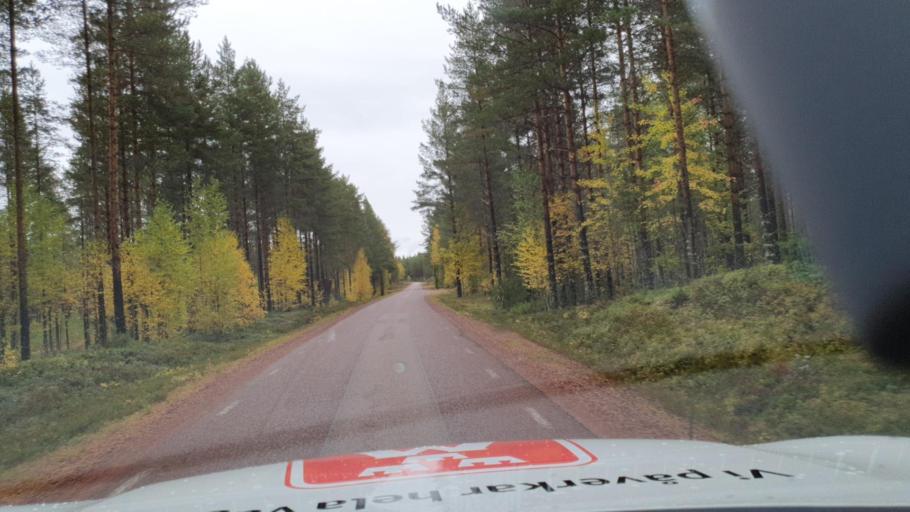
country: SE
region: Dalarna
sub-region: Alvdalens Kommun
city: AElvdalen
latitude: 61.2510
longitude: 14.0963
